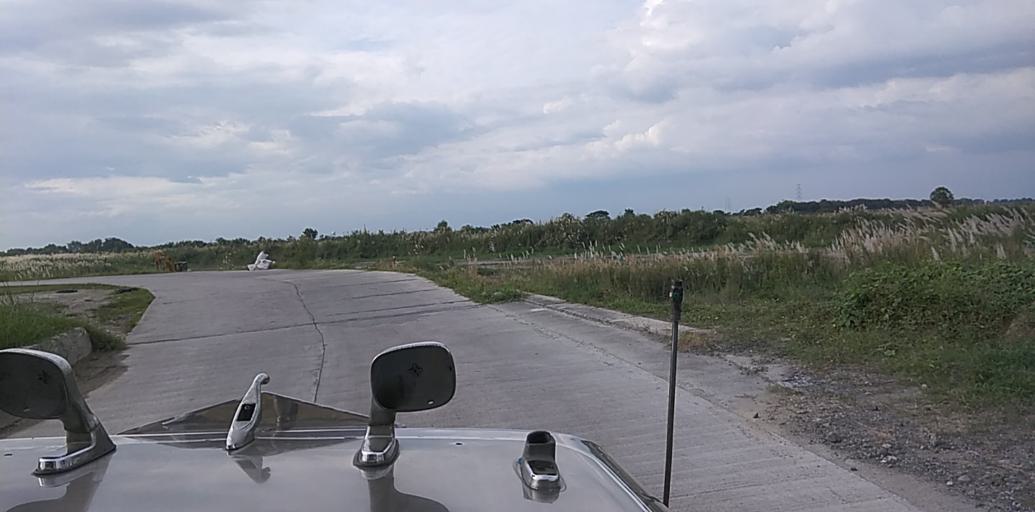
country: PH
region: Central Luzon
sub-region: Province of Pampanga
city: Minalin
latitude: 14.9673
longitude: 120.6626
